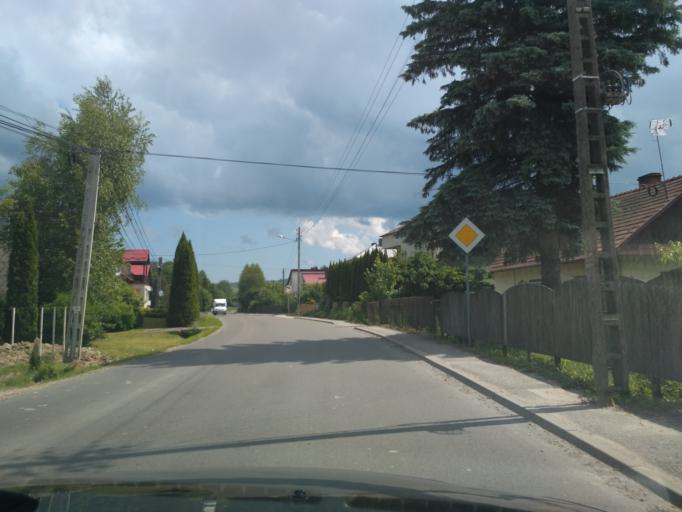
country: PL
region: Subcarpathian Voivodeship
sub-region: Powiat rzeszowski
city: Blazowa
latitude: 49.8790
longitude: 22.0862
